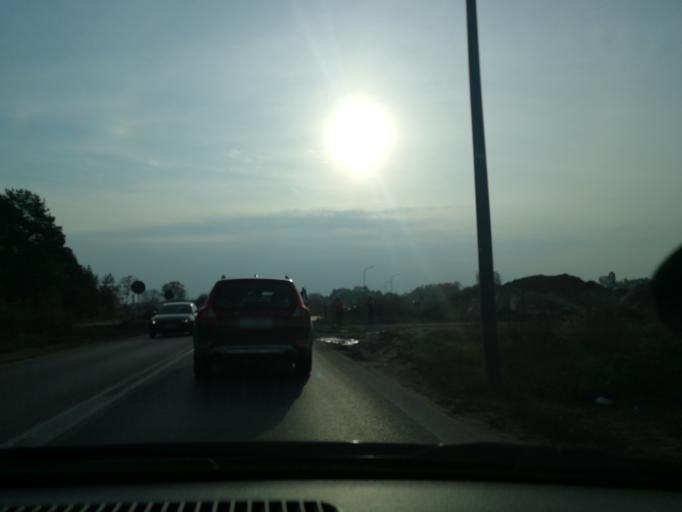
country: PL
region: Masovian Voivodeship
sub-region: Warszawa
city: Wawer
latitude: 52.1649
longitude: 21.1617
